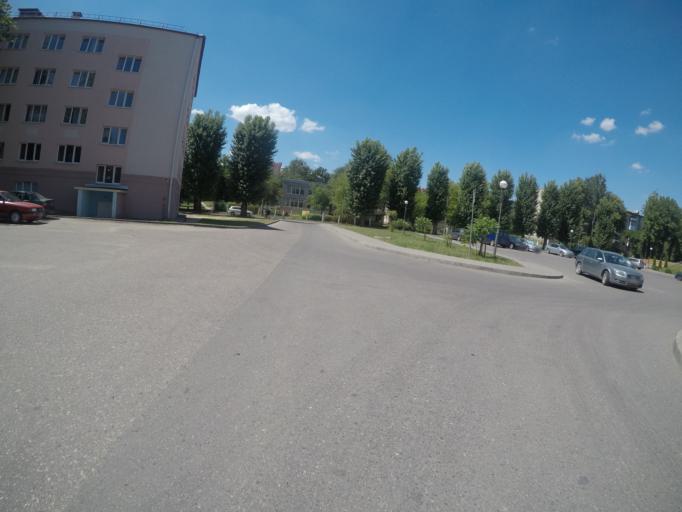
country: BY
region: Grodnenskaya
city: Hrodna
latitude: 53.6949
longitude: 23.8262
